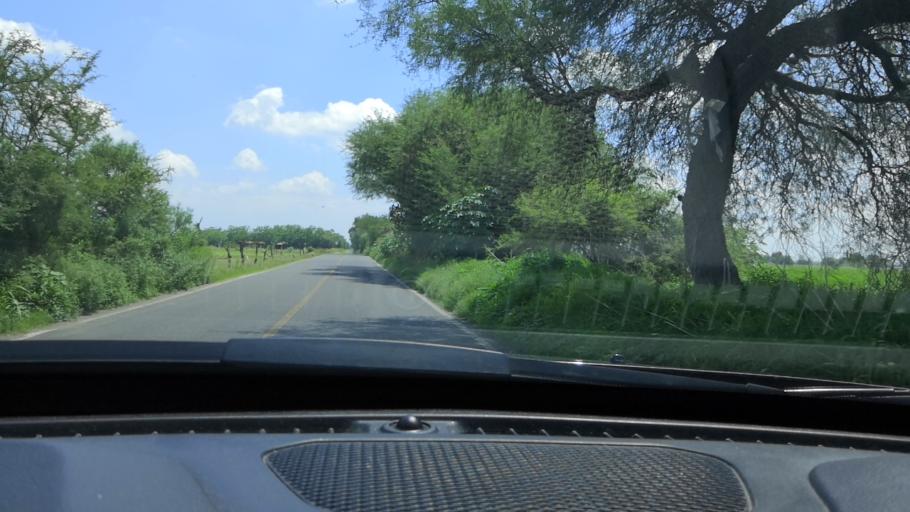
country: MX
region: Guanajuato
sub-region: Silao de la Victoria
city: El Refugio de los Sauces
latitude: 20.9631
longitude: -101.5857
